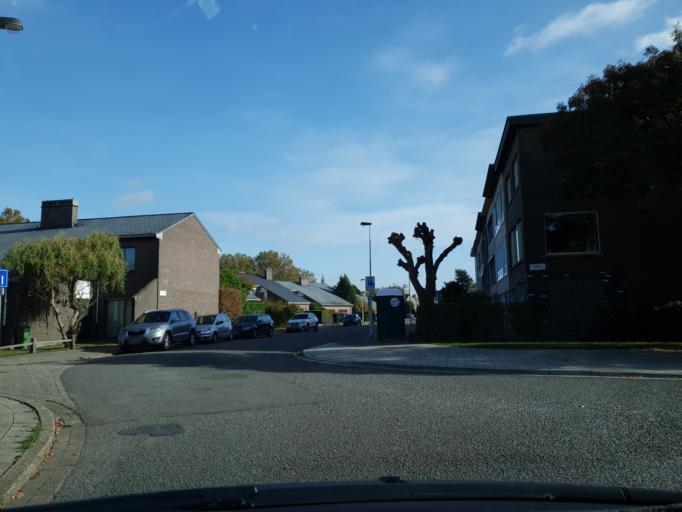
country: BE
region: Flanders
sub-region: Provincie Antwerpen
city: Antwerpen
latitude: 51.2175
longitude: 4.3806
